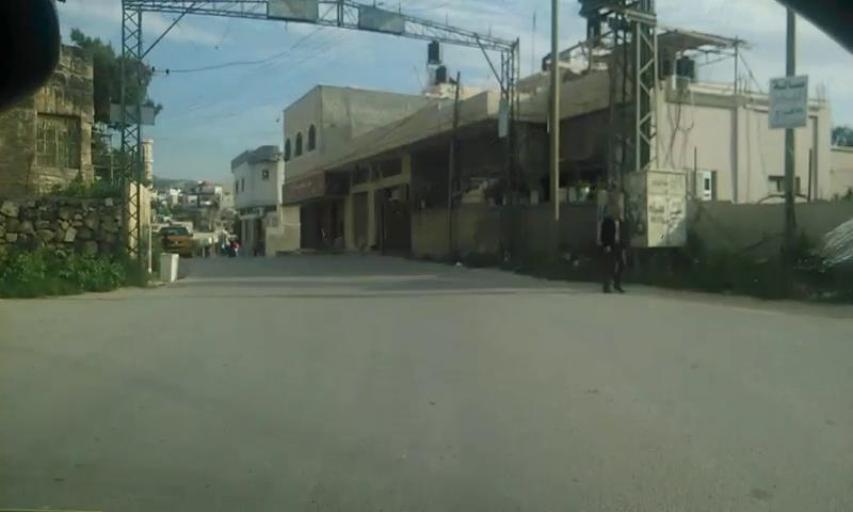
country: PS
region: West Bank
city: Nuba
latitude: 31.6099
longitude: 35.0345
